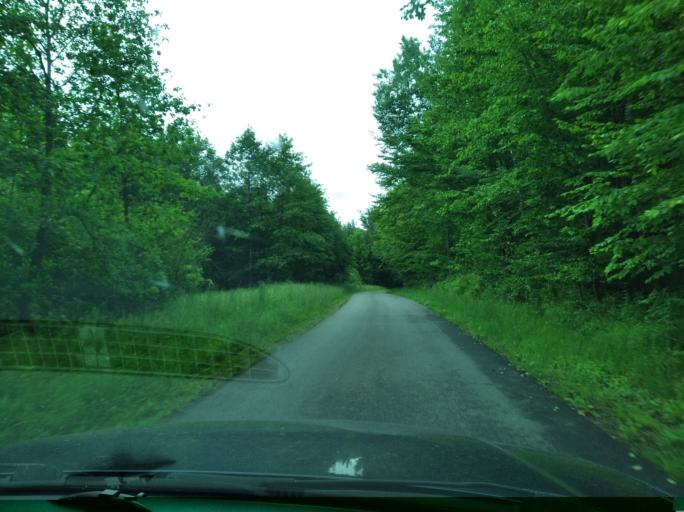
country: PL
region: Subcarpathian Voivodeship
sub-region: Powiat przemyski
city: Przedmiescie Dubieckie
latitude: 49.8743
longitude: 22.4040
